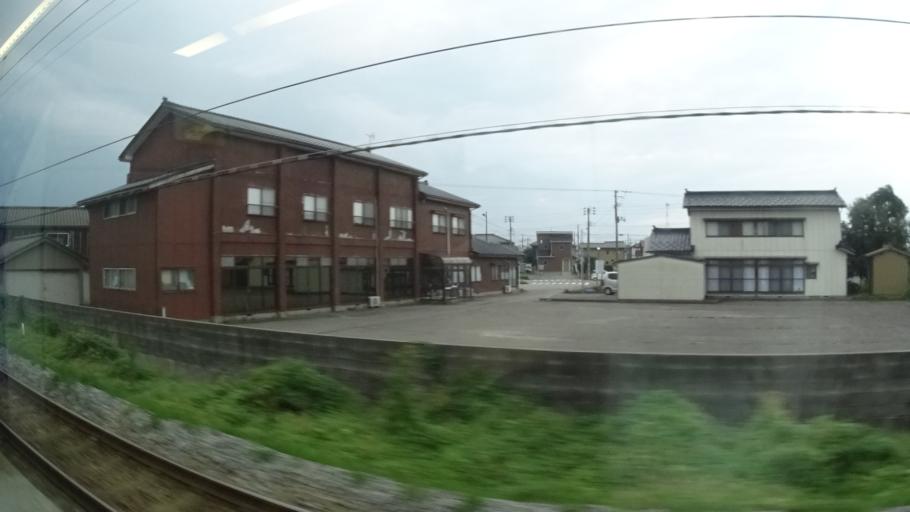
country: JP
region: Niigata
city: Murakami
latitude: 38.2281
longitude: 139.4616
